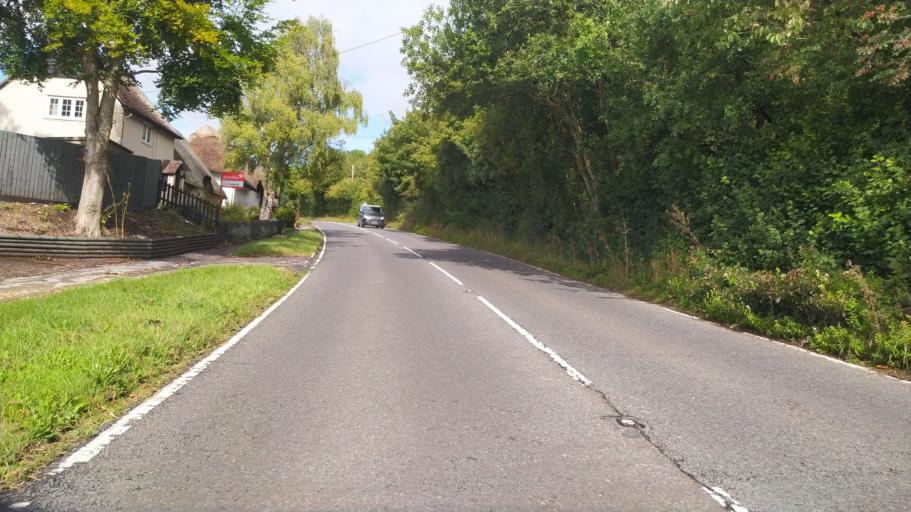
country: GB
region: England
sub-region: Dorset
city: Blandford Forum
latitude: 50.8421
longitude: -2.0986
